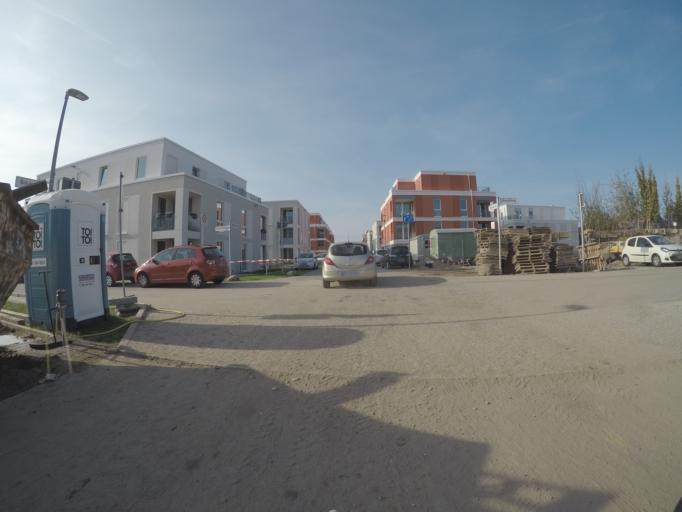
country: DE
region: Berlin
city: Altglienicke
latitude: 52.4129
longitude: 13.5319
